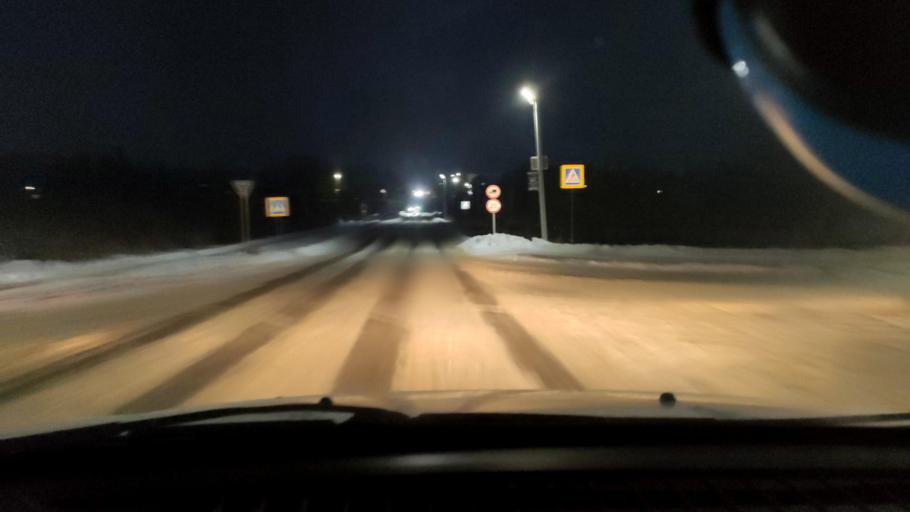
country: RU
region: Perm
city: Kultayevo
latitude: 57.9001
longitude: 55.9257
